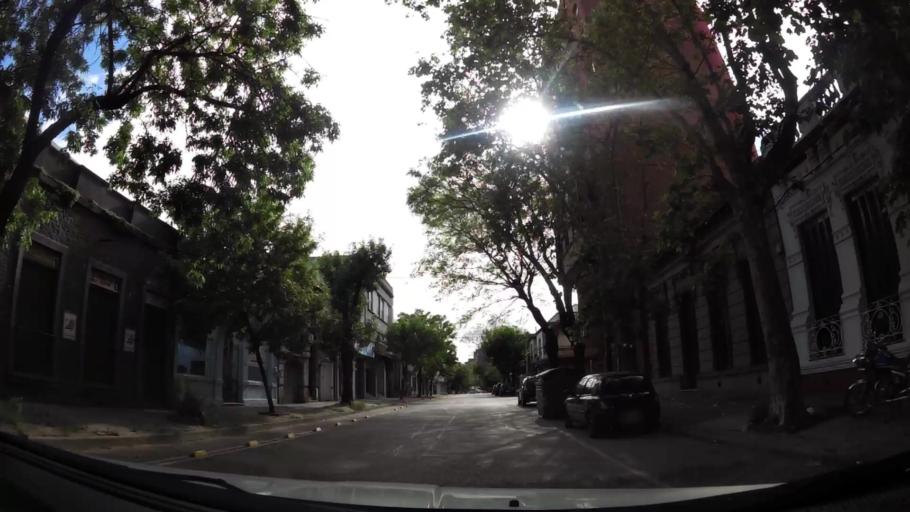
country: UY
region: Montevideo
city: Montevideo
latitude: -34.8892
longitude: -56.1691
